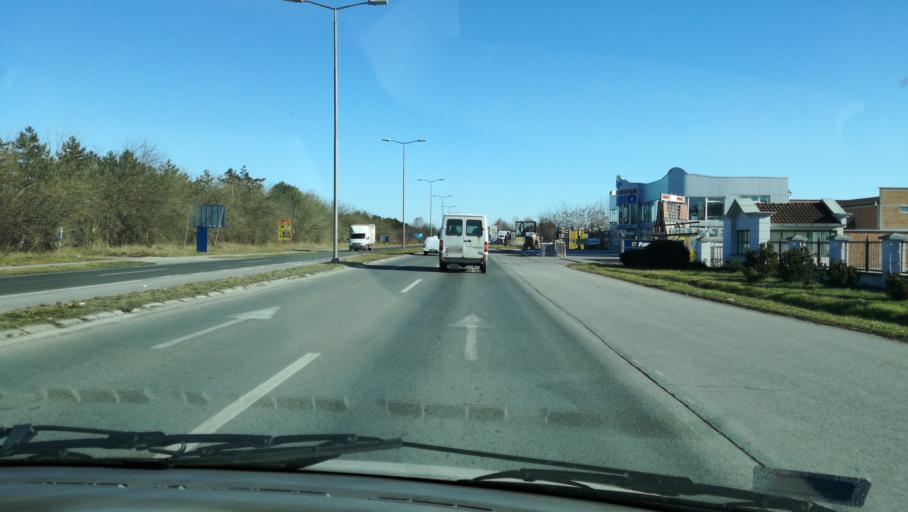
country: RS
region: Autonomna Pokrajina Vojvodina
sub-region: Severnobacki Okrug
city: Subotica
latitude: 46.1025
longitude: 19.7043
